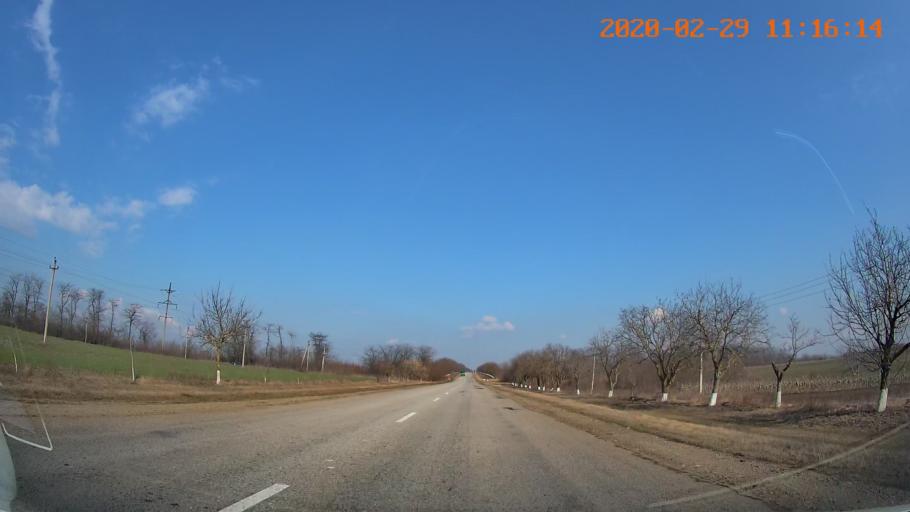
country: MD
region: Telenesti
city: Dubasari
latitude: 47.3057
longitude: 29.1672
